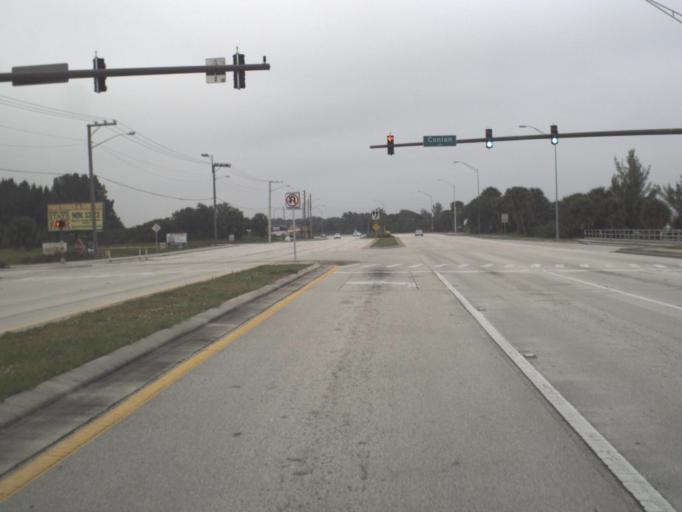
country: US
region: Florida
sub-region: Brevard County
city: Palm Bay
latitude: 28.0539
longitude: -80.5890
